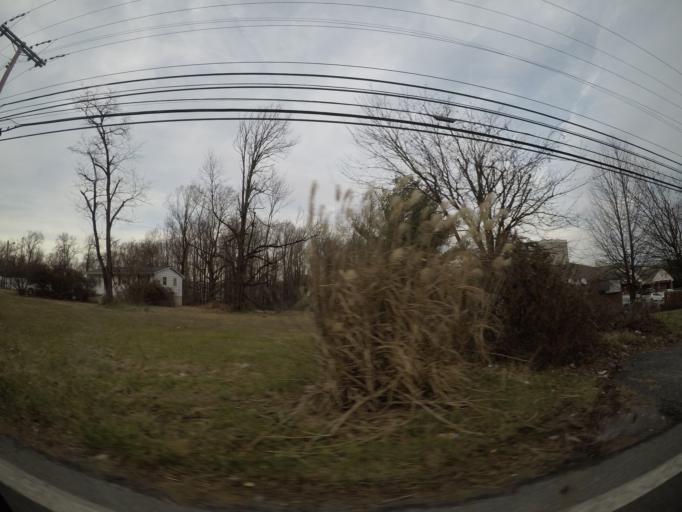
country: US
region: Maryland
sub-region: Anne Arundel County
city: Jessup
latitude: 39.1926
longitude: -76.7744
